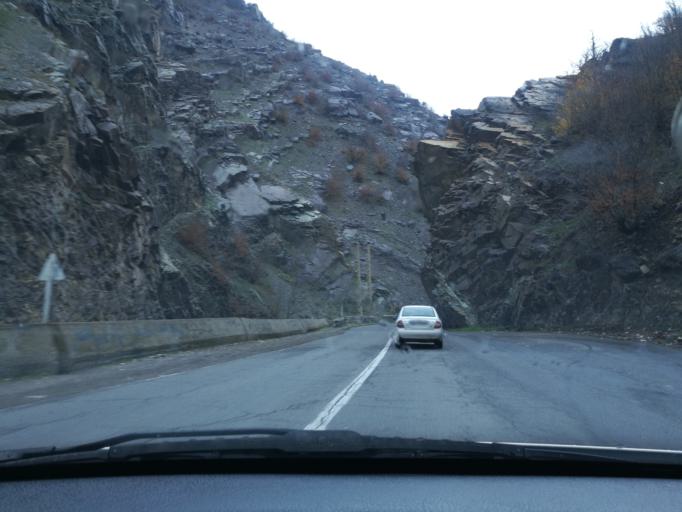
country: IR
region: Mazandaran
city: Chalus
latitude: 36.2793
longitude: 51.2425
